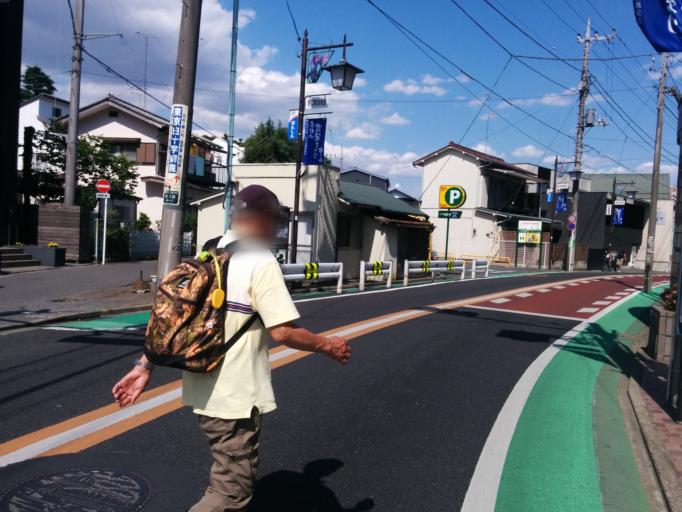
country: JP
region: Tokyo
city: Higashimurayama-shi
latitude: 35.7621
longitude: 139.4607
